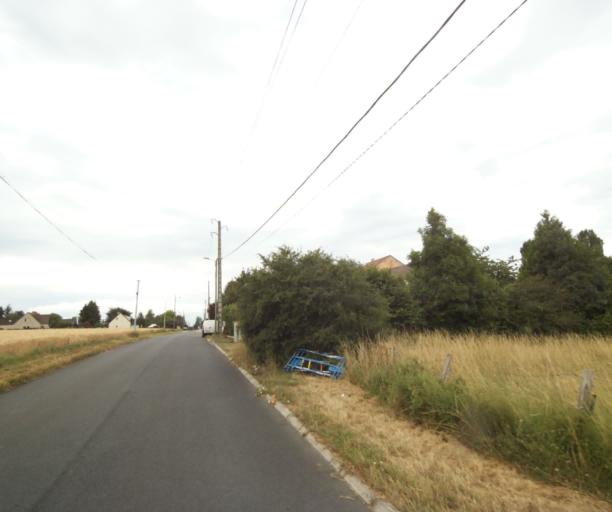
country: FR
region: Ile-de-France
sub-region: Departement de Seine-et-Marne
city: Saint-Sauveur-sur-Ecole
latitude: 48.4896
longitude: 2.5412
